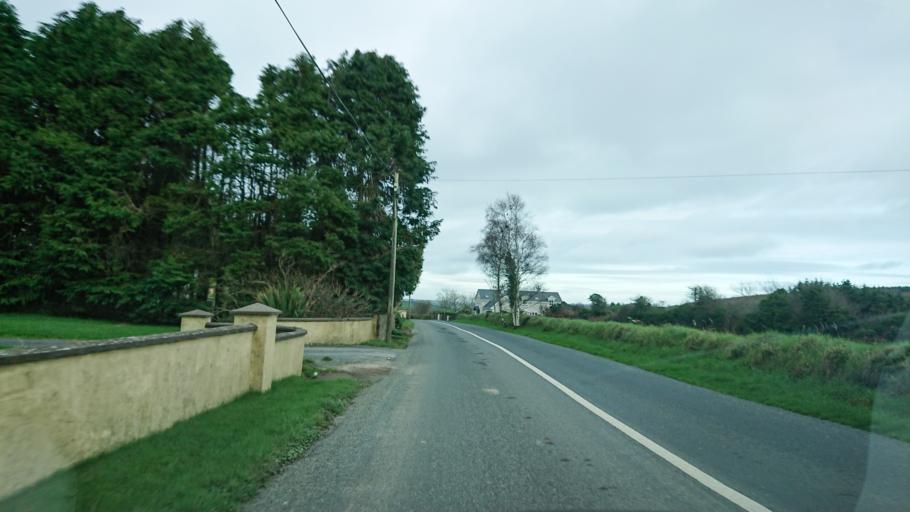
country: IE
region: Leinster
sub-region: Kilkenny
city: Mooncoin
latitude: 52.2065
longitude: -7.2496
